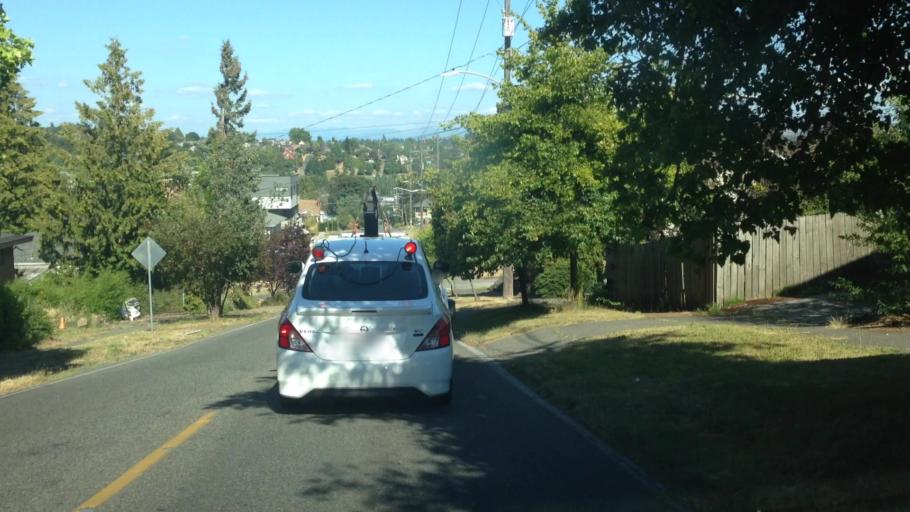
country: US
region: Washington
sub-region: King County
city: Seattle
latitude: 47.5830
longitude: -122.3093
